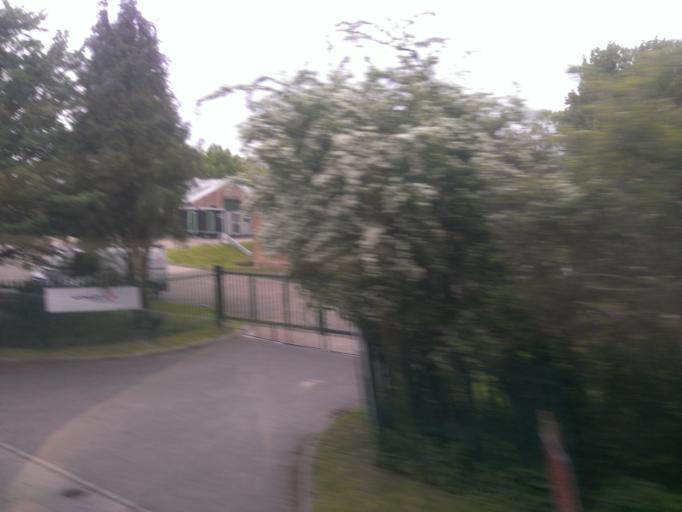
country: GB
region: England
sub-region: Suffolk
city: East Bergholt
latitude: 51.9547
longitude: 0.9620
